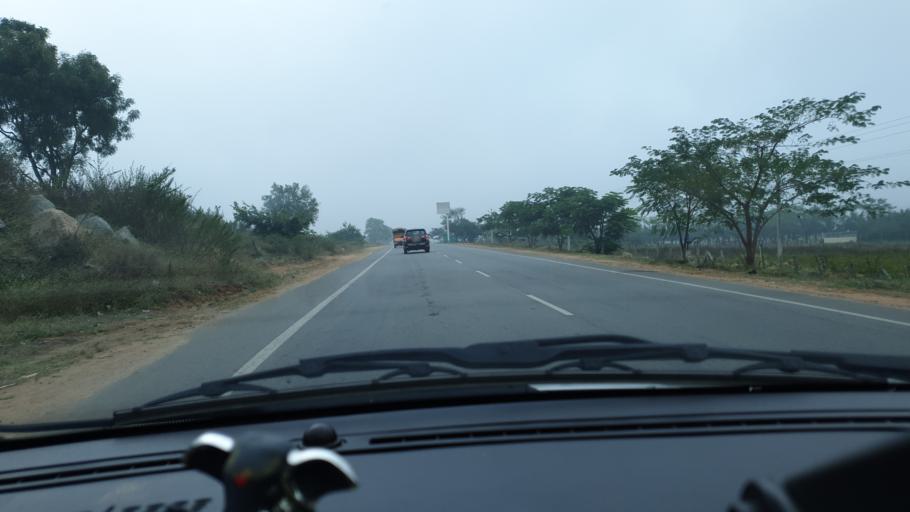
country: IN
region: Telangana
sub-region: Mahbubnagar
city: Farrukhnagar
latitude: 16.9636
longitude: 78.5108
